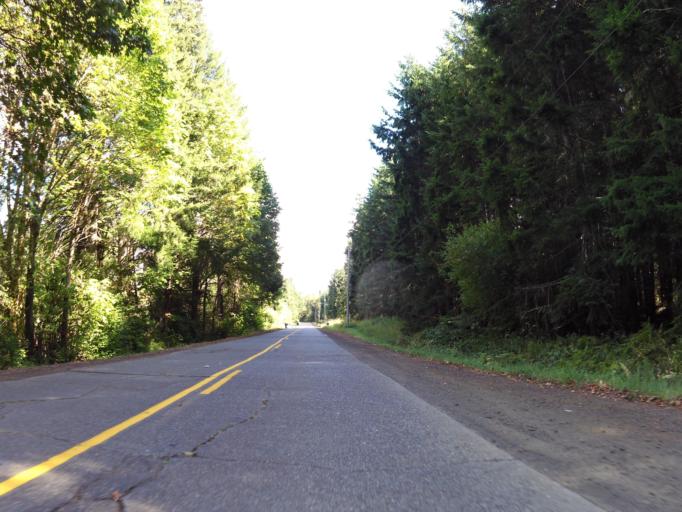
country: US
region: Washington
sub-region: Mason County
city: Shelton
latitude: 47.0944
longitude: -123.0895
